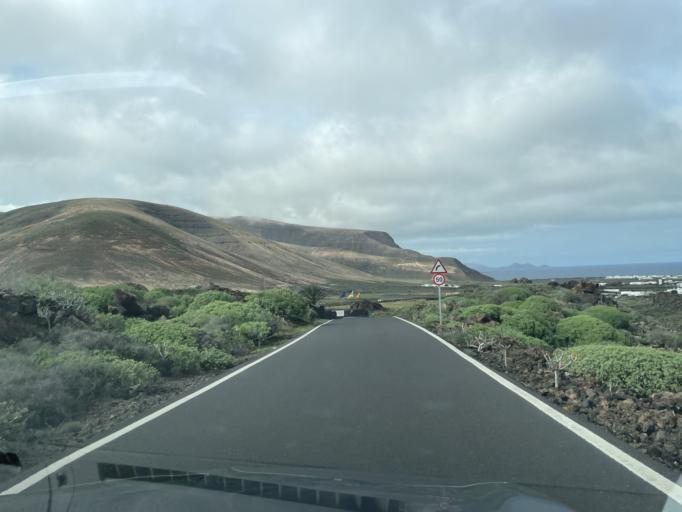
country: ES
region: Canary Islands
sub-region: Provincia de Las Palmas
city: Haria
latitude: 29.1997
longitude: -13.4518
